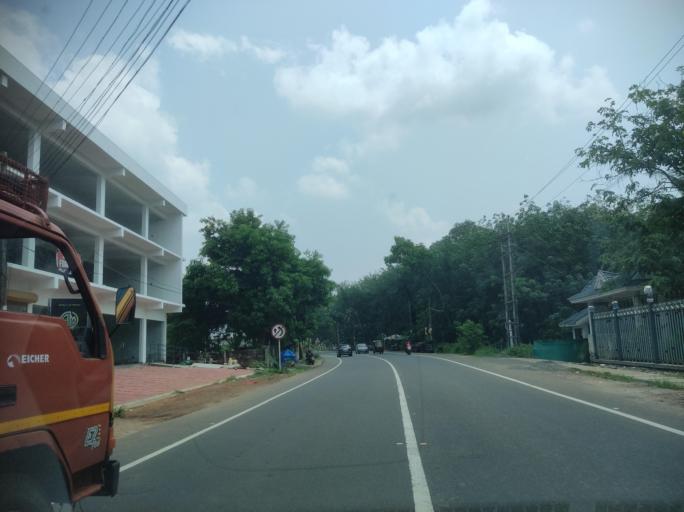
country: IN
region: Kerala
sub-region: Kottayam
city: Changanacheri
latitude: 9.4229
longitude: 76.5463
